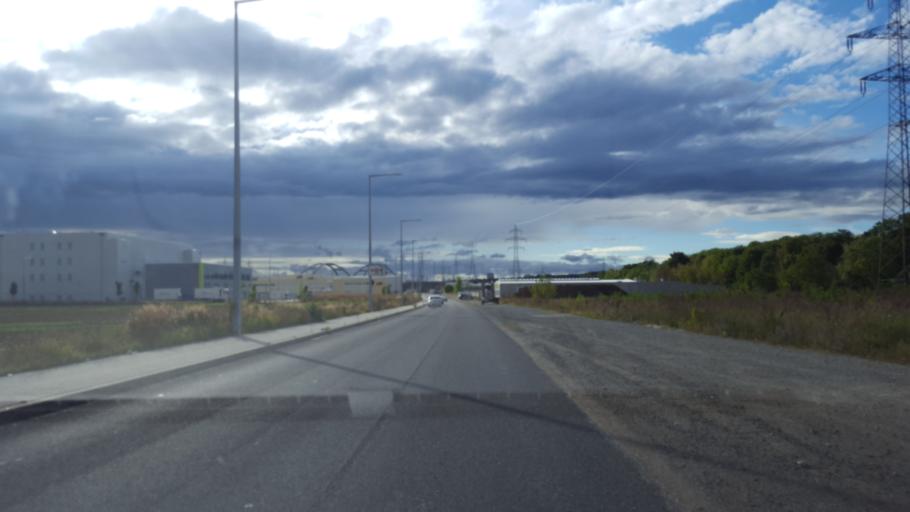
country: AT
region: Lower Austria
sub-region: Politischer Bezirk Wien-Umgebung
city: Schwechat
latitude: 48.1403
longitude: 16.4441
